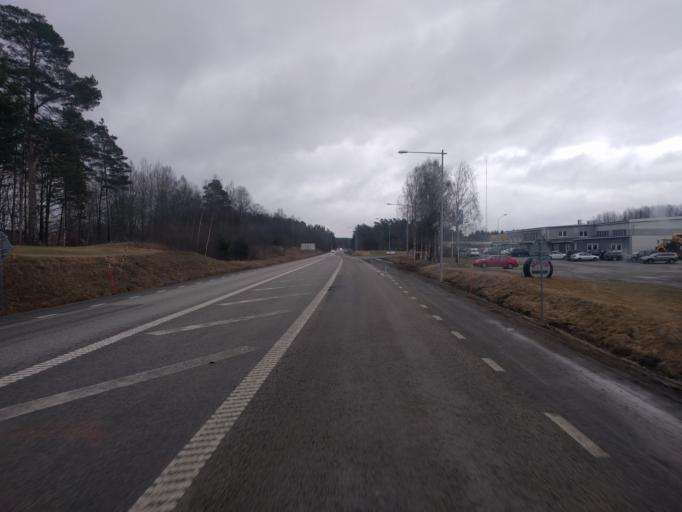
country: SE
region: Joenkoeping
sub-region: Eksjo Kommun
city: Eksjoe
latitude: 57.6630
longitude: 14.9930
